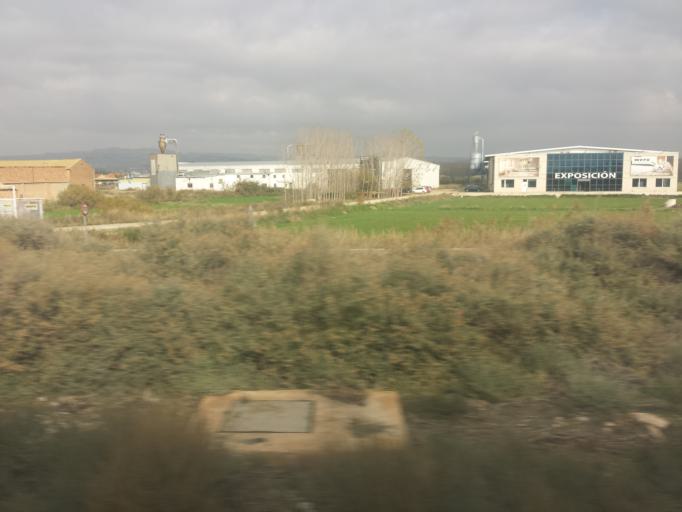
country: ES
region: Aragon
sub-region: Provincia de Zaragoza
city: Figueruelas
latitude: 41.7872
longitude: -1.1654
